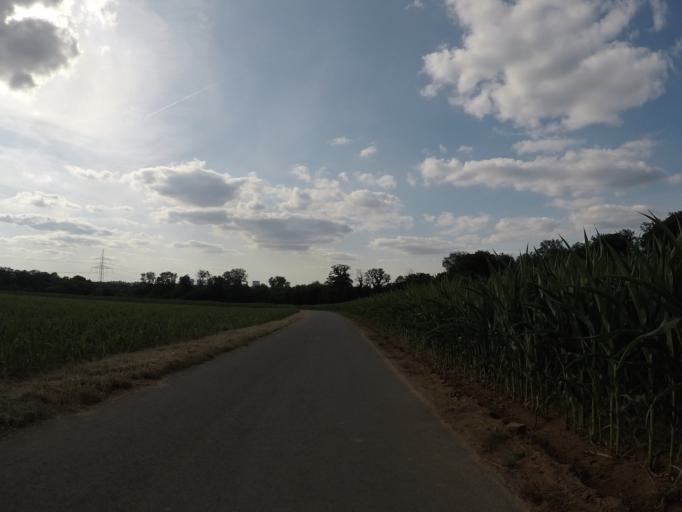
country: LU
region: Luxembourg
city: Itzig
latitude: 49.6048
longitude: 6.1777
